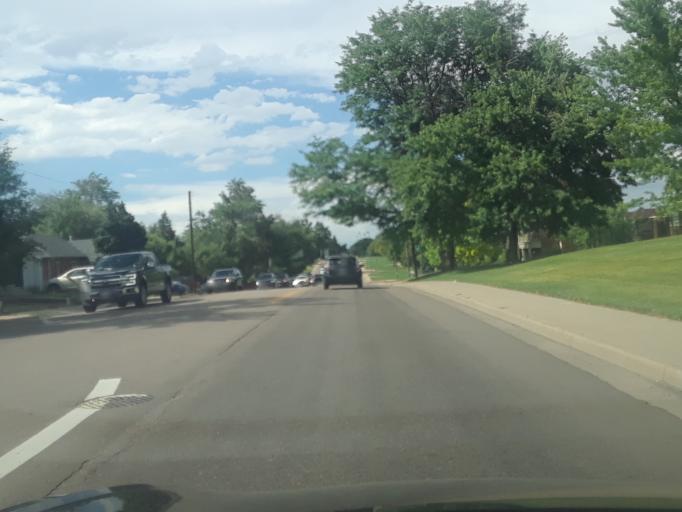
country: US
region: Colorado
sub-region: Arapahoe County
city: Glendale
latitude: 39.7279
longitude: -104.9034
